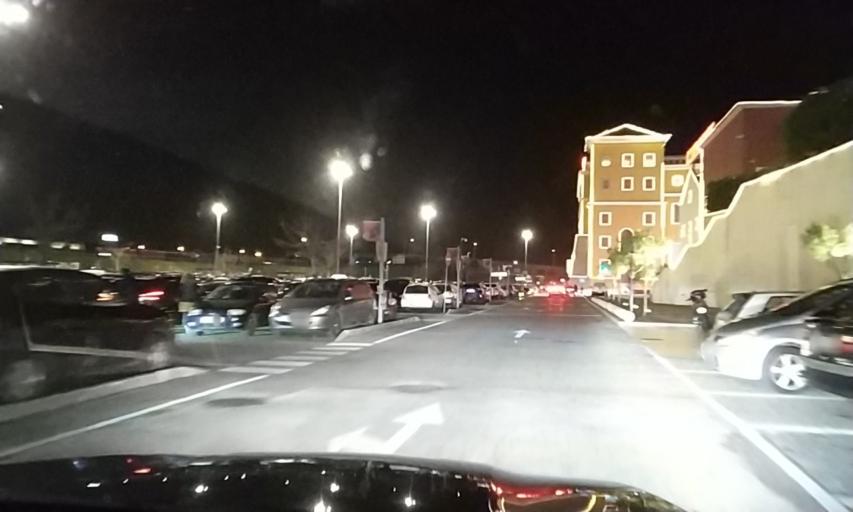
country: PT
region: Setubal
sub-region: Montijo
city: Montijo
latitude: 38.6955
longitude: -8.9414
